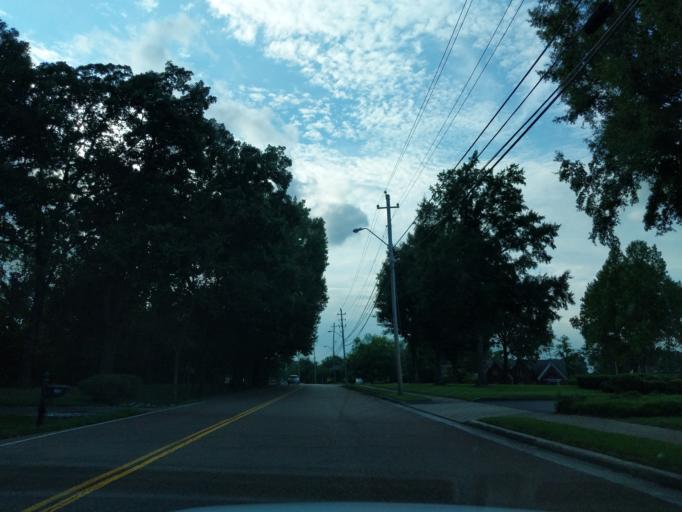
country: US
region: Tennessee
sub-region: Shelby County
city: Germantown
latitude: 35.0657
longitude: -89.7688
